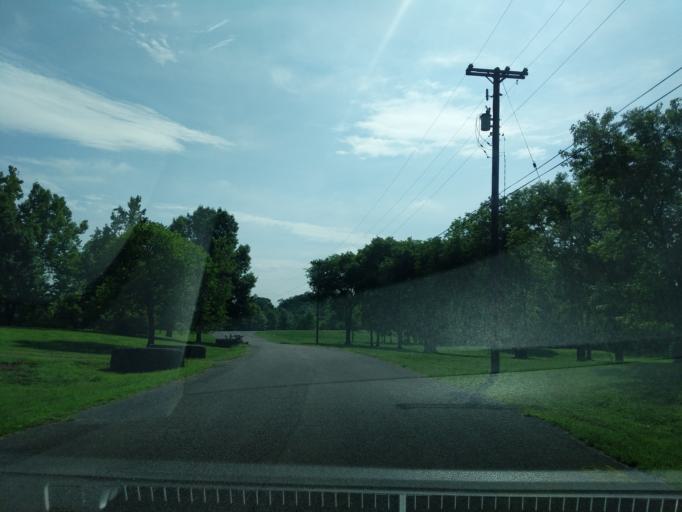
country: US
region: Tennessee
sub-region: Davidson County
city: Goodlettsville
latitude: 36.3142
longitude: -86.6674
